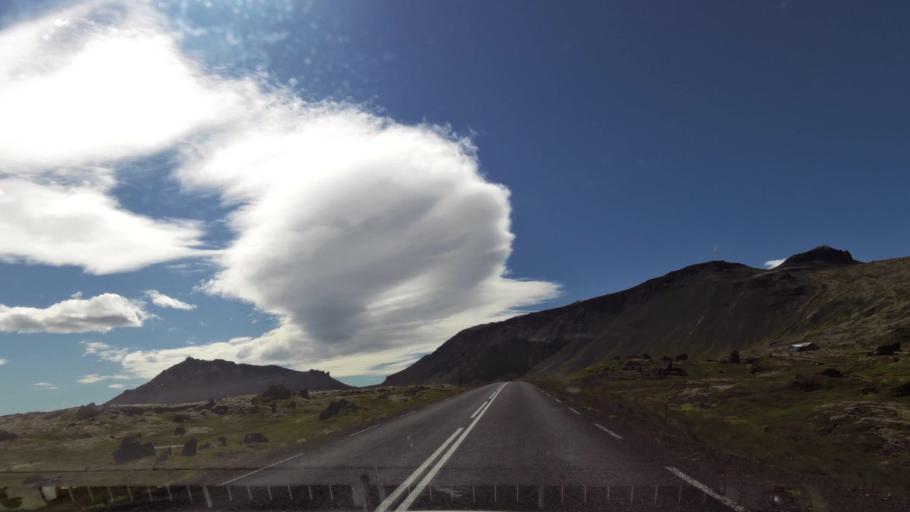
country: IS
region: West
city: Olafsvik
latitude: 64.8072
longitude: -23.6090
